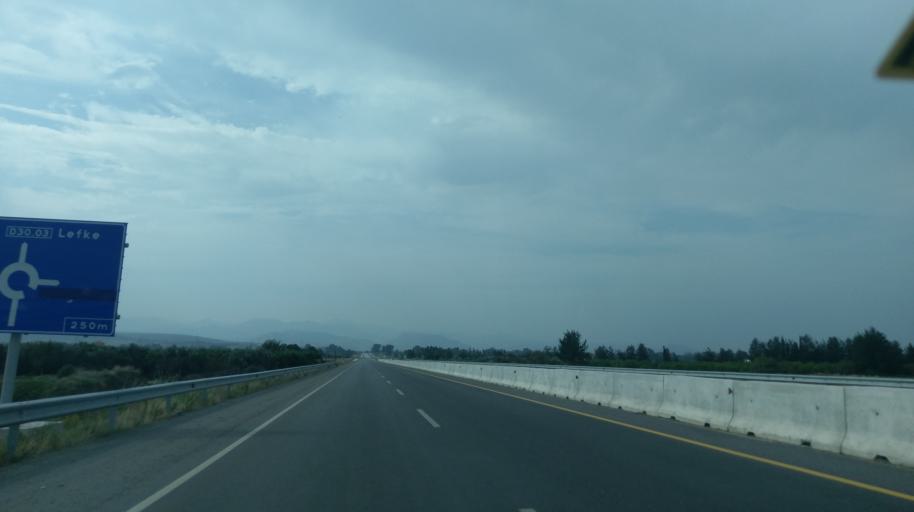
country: CY
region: Lefkosia
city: Lefka
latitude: 35.1558
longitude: 32.9112
